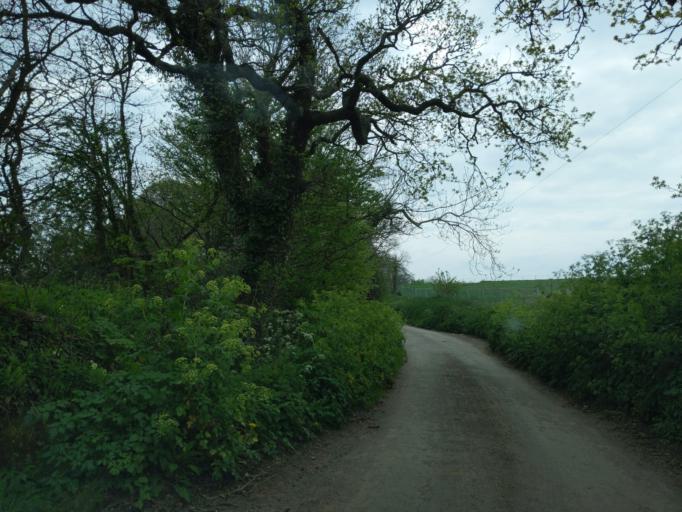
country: GB
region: England
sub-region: Devon
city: Yealmpton
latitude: 50.3602
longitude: -4.0295
